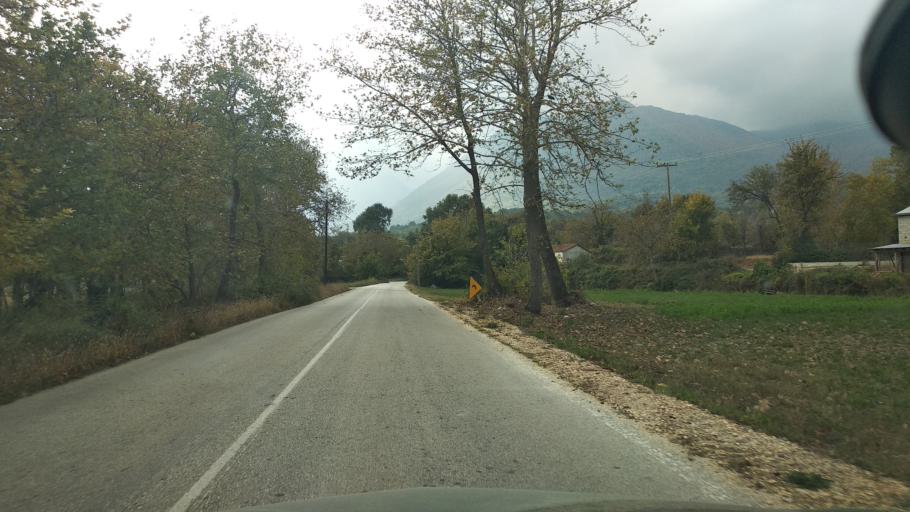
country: GR
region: Thessaly
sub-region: Trikala
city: Kastraki
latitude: 39.6974
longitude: 21.5232
